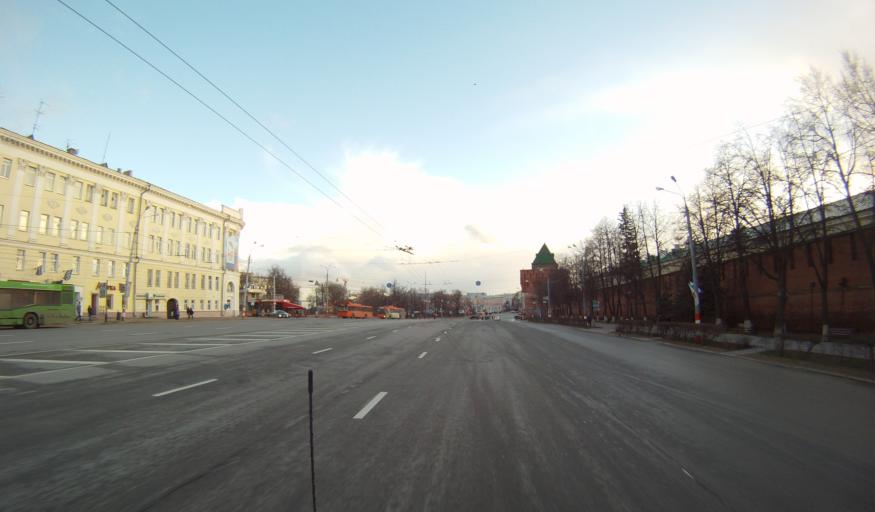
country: RU
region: Nizjnij Novgorod
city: Nizhniy Novgorod
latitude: 56.3282
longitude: 44.0074
